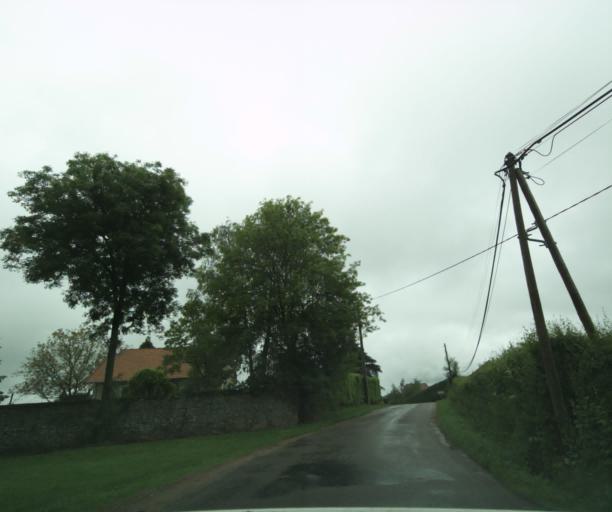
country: FR
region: Bourgogne
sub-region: Departement de Saone-et-Loire
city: Charolles
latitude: 46.4377
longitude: 4.3395
